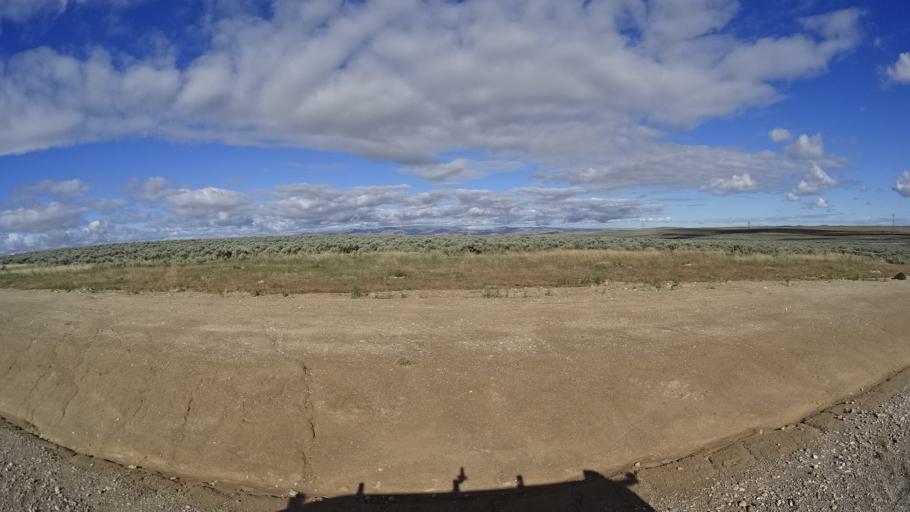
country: US
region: Idaho
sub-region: Ada County
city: Kuna
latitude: 43.3296
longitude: -116.4140
